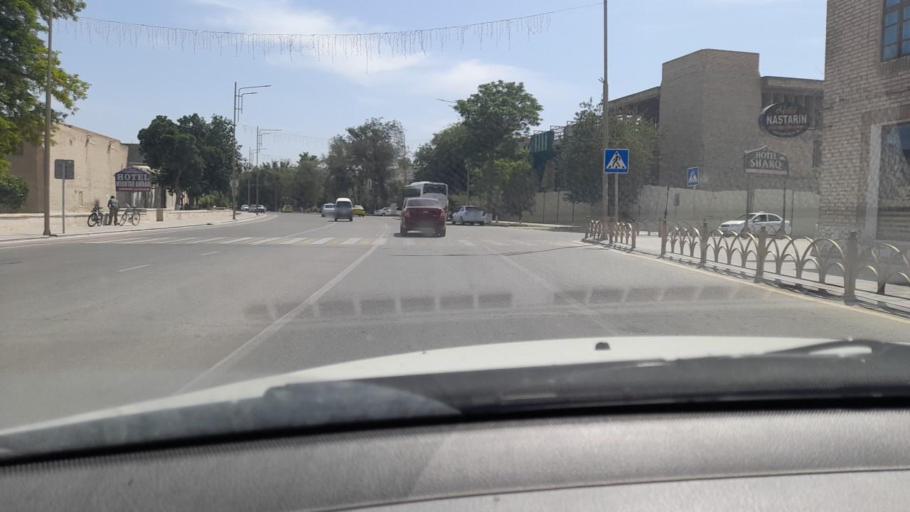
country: UZ
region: Bukhara
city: Bukhara
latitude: 39.7729
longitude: 64.4261
